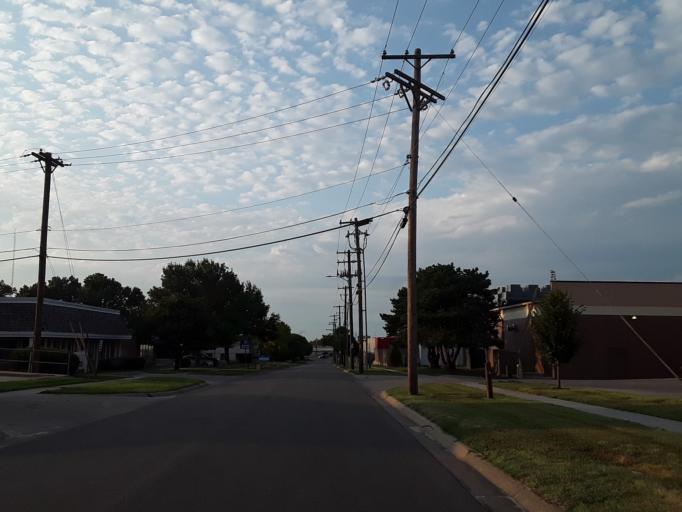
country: US
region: Nebraska
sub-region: Lancaster County
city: Lincoln
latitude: 40.8140
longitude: -96.6561
